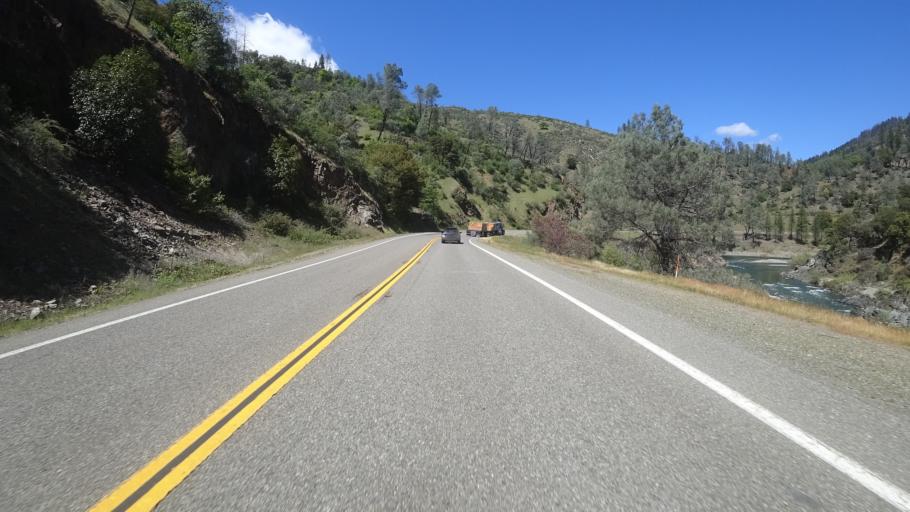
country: US
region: California
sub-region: Trinity County
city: Weaverville
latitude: 40.7675
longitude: -123.1369
